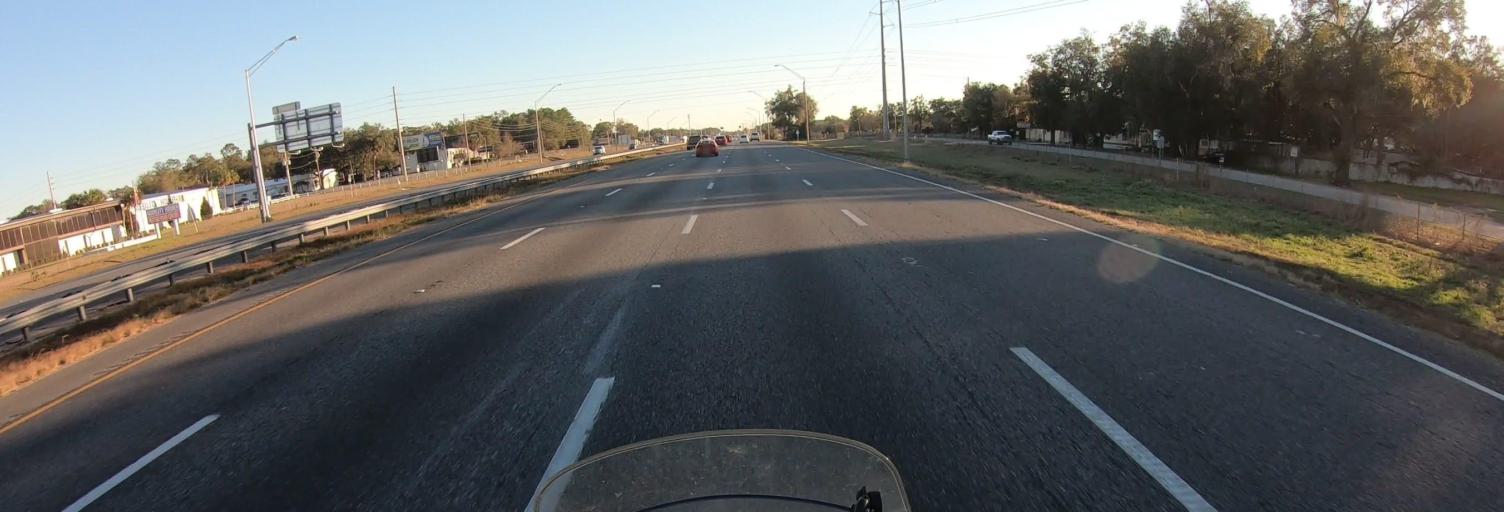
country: US
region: Florida
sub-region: Marion County
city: Ocala
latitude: 29.1827
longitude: -82.1838
